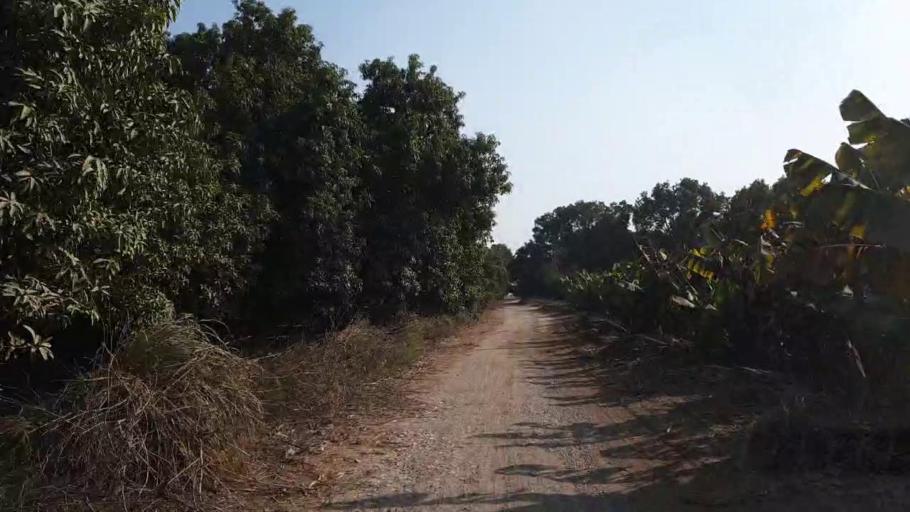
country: PK
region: Sindh
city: Tando Adam
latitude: 25.6045
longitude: 68.6148
